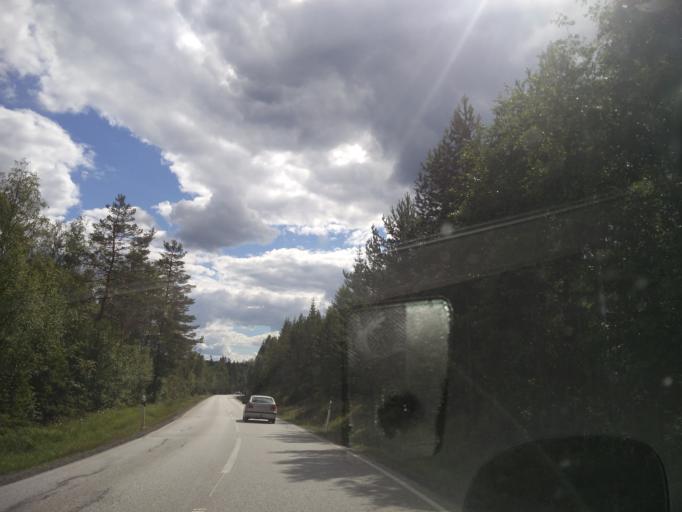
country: SE
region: OErebro
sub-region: Ljusnarsbergs Kommun
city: Kopparberg
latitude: 59.8407
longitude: 14.9969
